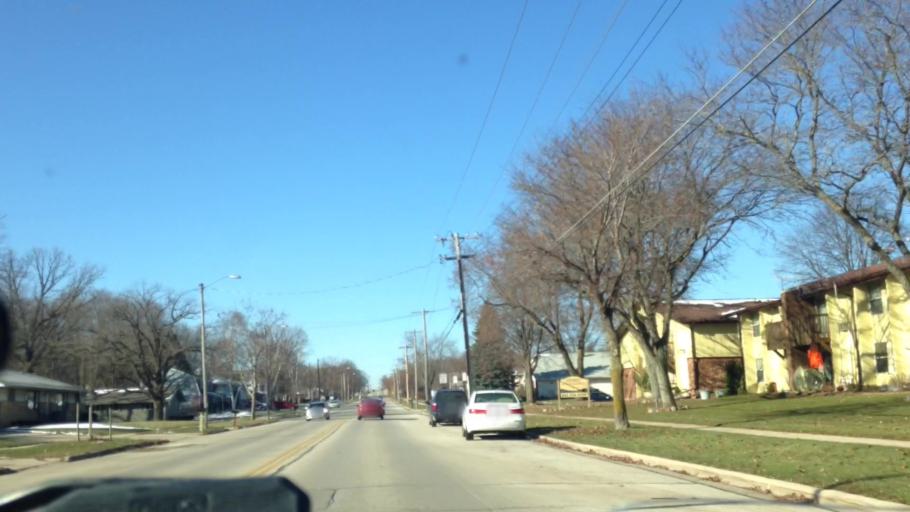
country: US
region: Wisconsin
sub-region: Washington County
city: West Bend
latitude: 43.3977
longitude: -88.1696
